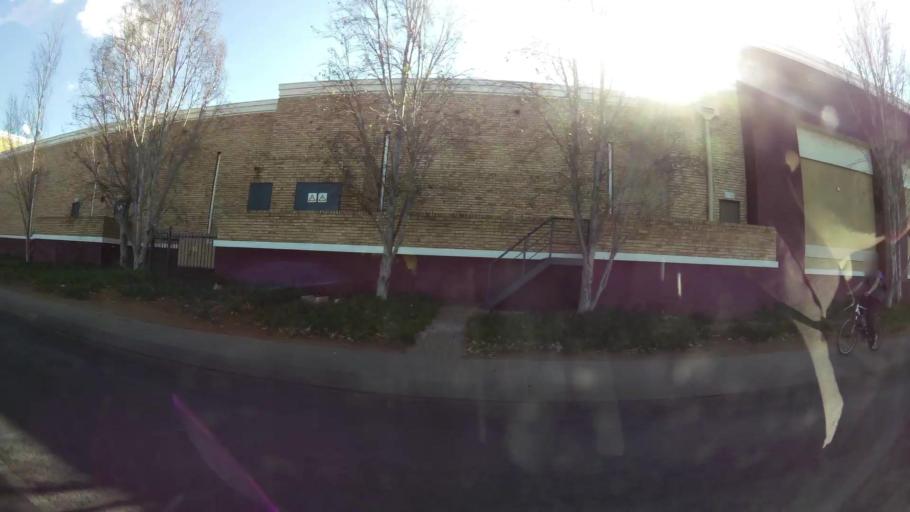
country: ZA
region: Northern Cape
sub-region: Frances Baard District Municipality
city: Kimberley
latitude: -28.7650
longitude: 24.7658
